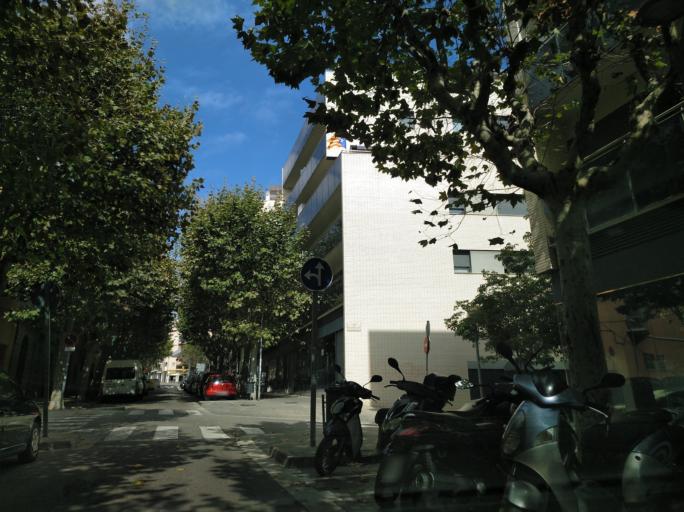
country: ES
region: Catalonia
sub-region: Provincia de Barcelona
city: Mataro
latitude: 41.5448
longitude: 2.4480
